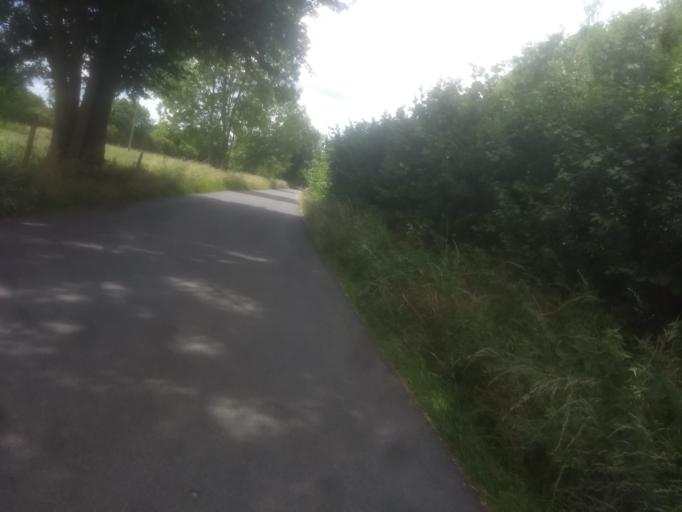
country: FR
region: Nord-Pas-de-Calais
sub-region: Departement du Pas-de-Calais
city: Maroeuil
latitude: 50.3303
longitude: 2.6911
